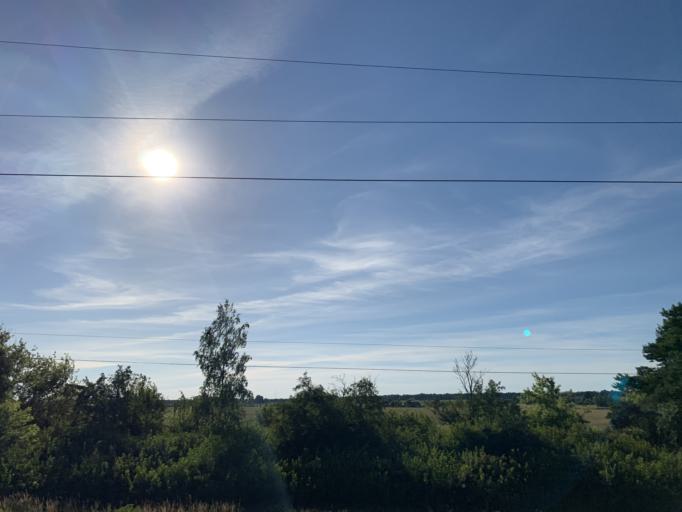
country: BY
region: Minsk
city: Haradzyeya
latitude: 53.3794
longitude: 26.5906
